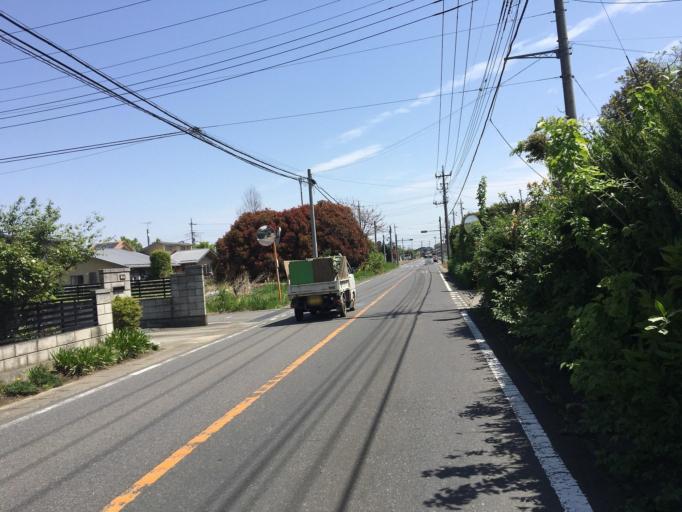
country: JP
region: Gunma
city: Sakai-nakajima
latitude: 36.2797
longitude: 139.2921
